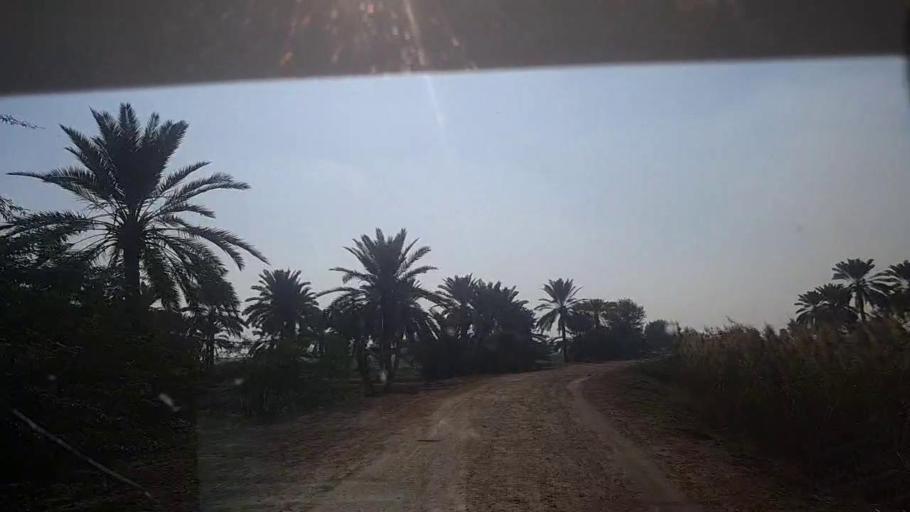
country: PK
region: Sindh
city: Gambat
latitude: 27.3755
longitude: 68.5742
